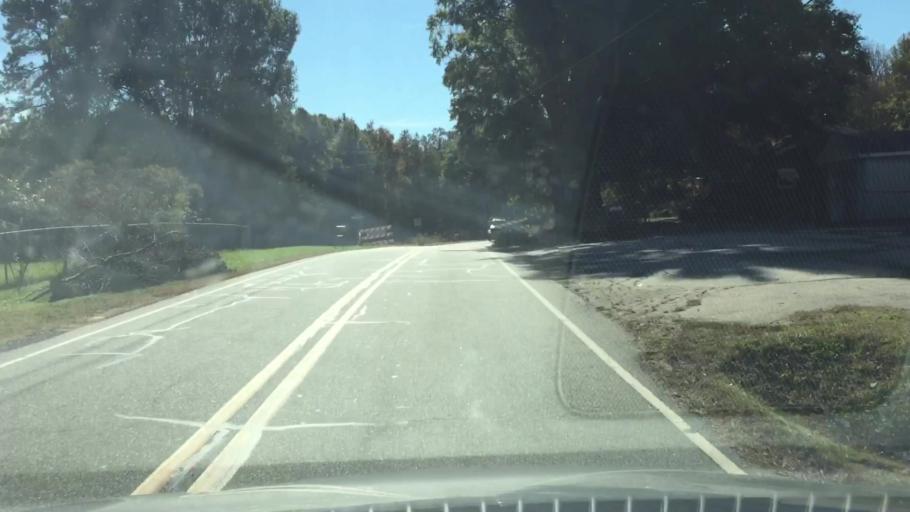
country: US
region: North Carolina
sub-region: Rockingham County
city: Reidsville
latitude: 36.3206
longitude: -79.6289
